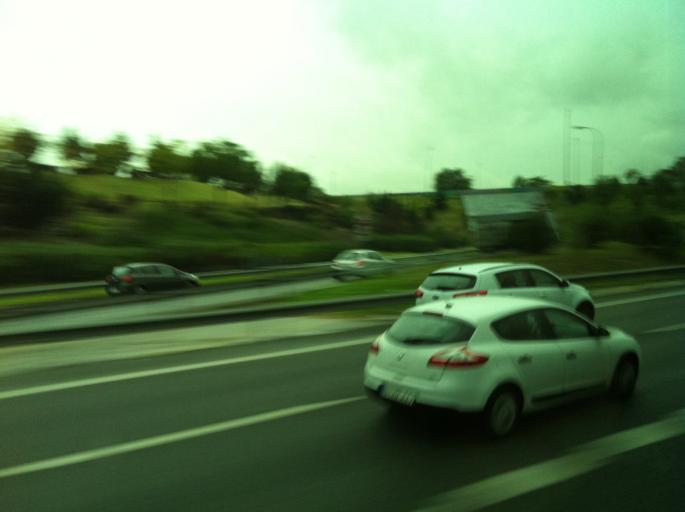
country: ES
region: Madrid
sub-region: Provincia de Madrid
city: Usera
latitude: 40.3832
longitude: -3.6874
